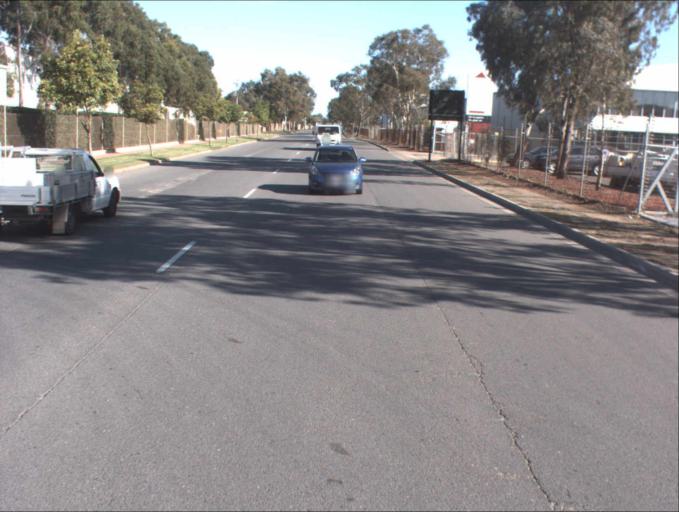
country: AU
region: South Australia
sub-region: Charles Sturt
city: Woodville North
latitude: -34.8408
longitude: 138.5566
